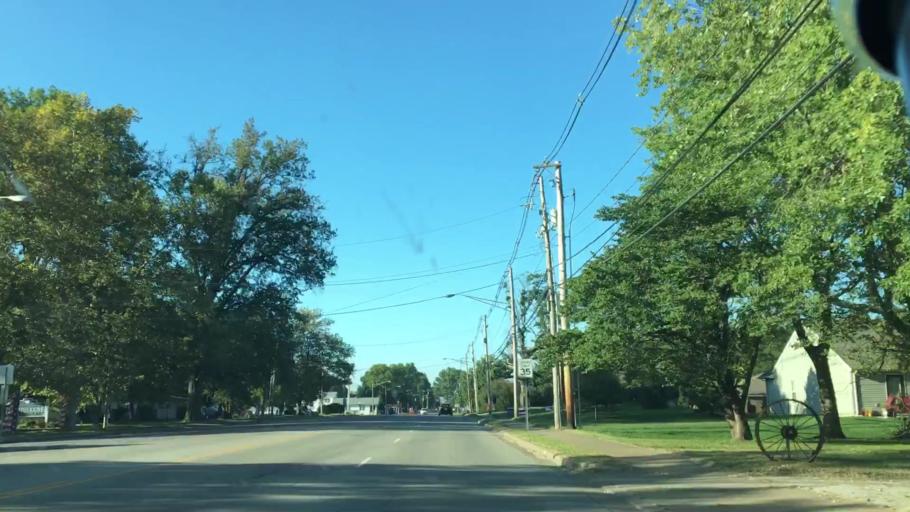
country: US
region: Indiana
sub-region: Vanderburgh County
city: Evansville
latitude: 37.9440
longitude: -87.4929
